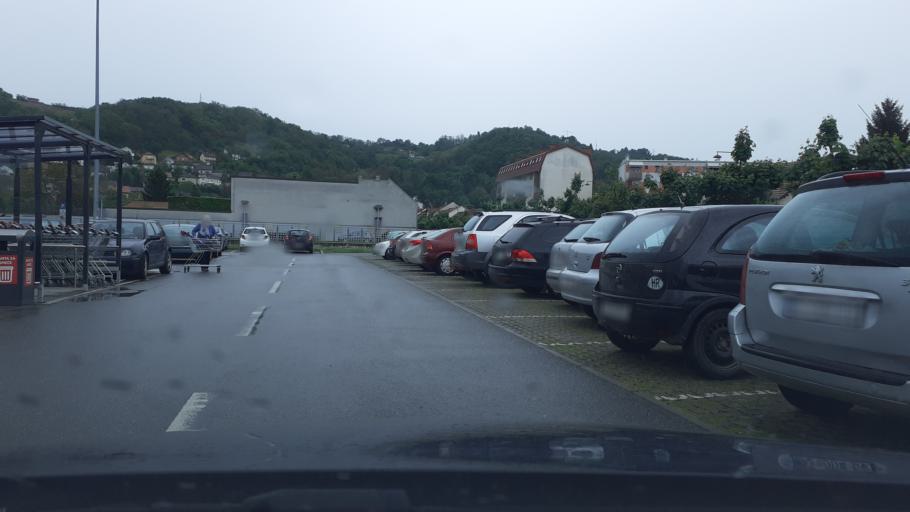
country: HR
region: Pozesko-Slavonska
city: Pozega
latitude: 45.3367
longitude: 17.6836
